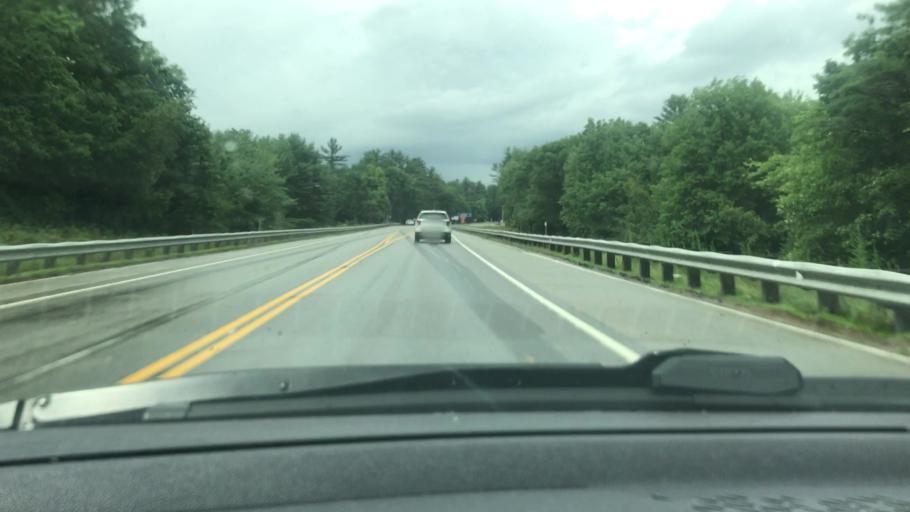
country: US
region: New Hampshire
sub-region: Merrimack County
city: Chichester
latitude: 43.2712
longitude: -71.4605
